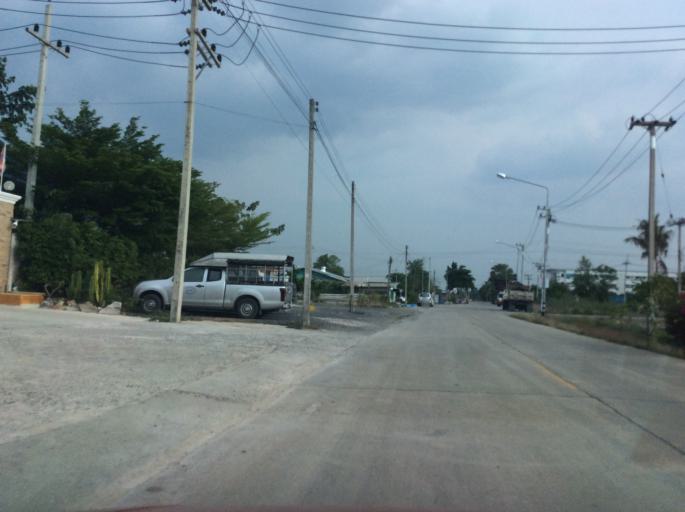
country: TH
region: Pathum Thani
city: Thanyaburi
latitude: 13.9875
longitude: 100.7275
